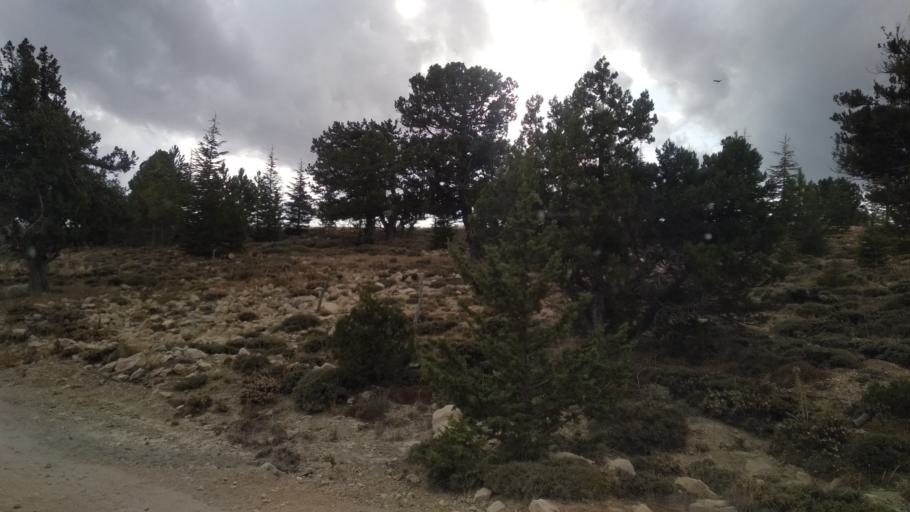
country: TR
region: Mersin
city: Sarikavak
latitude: 36.5725
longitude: 33.7494
